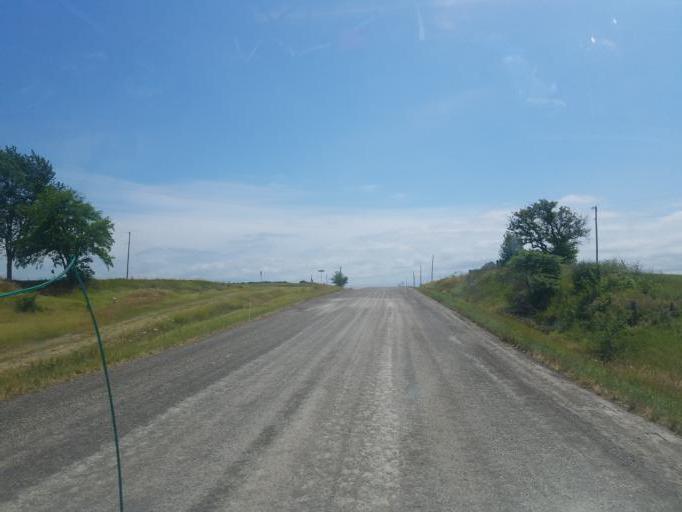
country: US
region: Indiana
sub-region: Allen County
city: Woodburn
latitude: 41.1648
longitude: -84.8490
